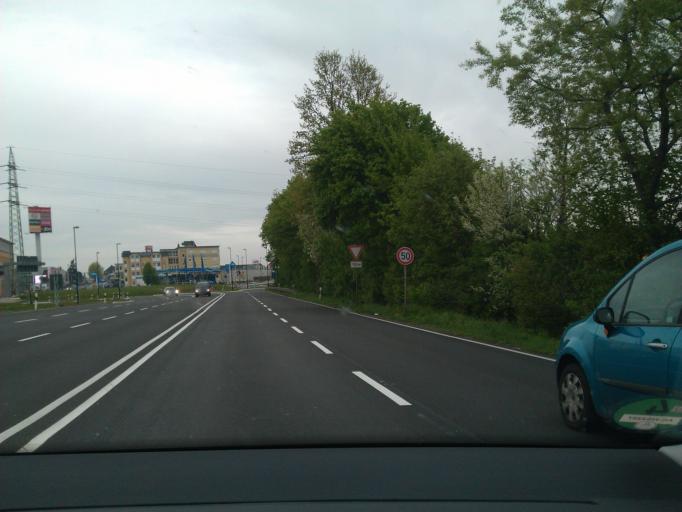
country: DE
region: North Rhine-Westphalia
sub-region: Regierungsbezirk Koln
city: Kerpen
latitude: 50.8951
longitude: 6.6856
